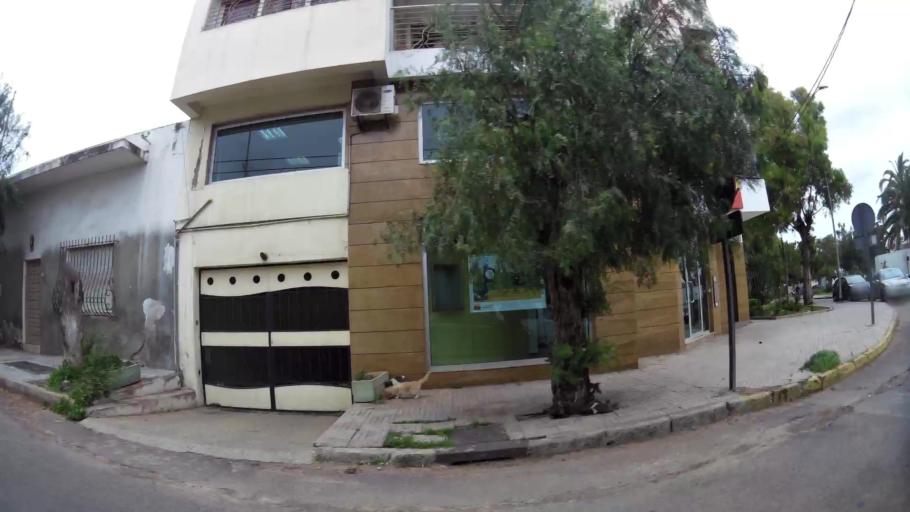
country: MA
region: Grand Casablanca
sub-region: Casablanca
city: Casablanca
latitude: 33.5562
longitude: -7.6351
